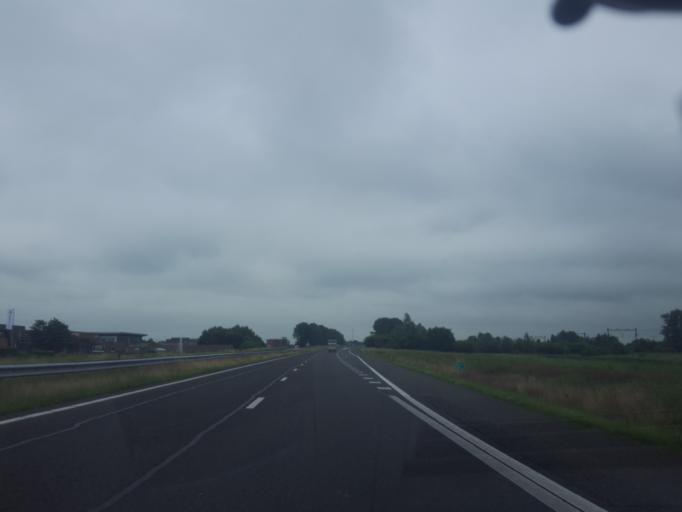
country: NL
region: Friesland
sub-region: Gemeente Boarnsterhim
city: Grou
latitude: 53.0971
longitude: 5.8201
